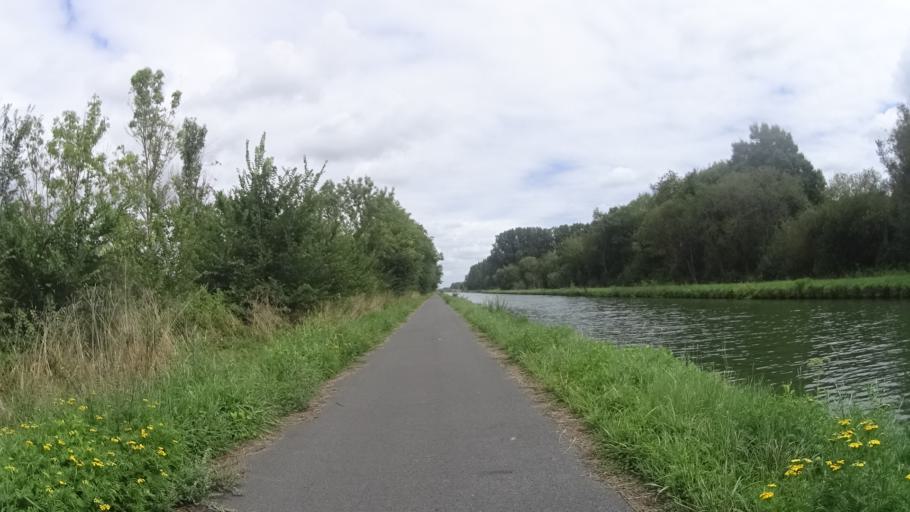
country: FR
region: Picardie
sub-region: Departement de l'Aisne
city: Ognes
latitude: 49.5867
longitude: 3.1755
